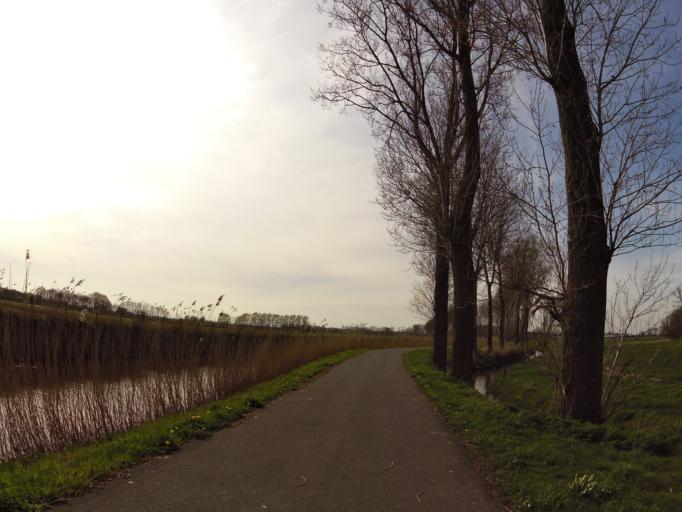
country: BE
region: Flanders
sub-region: Provincie West-Vlaanderen
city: Oudenburg
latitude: 51.1518
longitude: 3.0158
